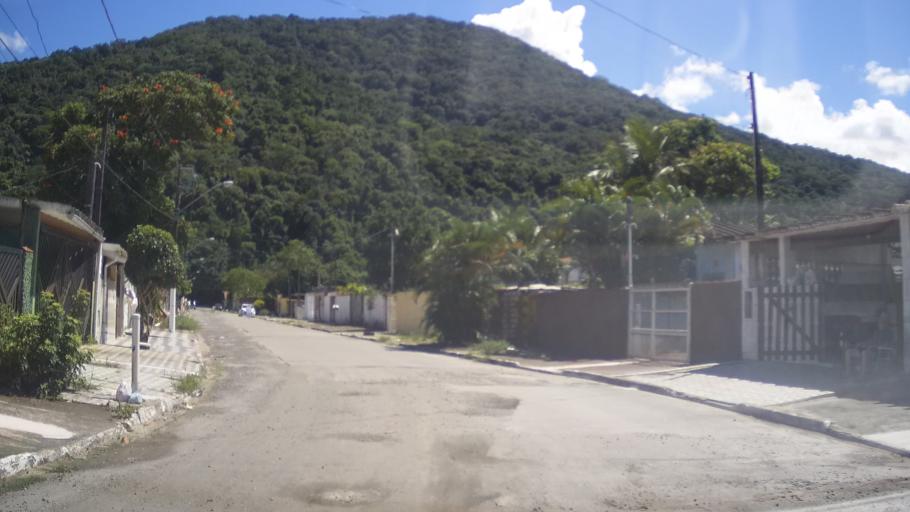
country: BR
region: Sao Paulo
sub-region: Mongagua
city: Mongagua
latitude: -24.0758
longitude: -46.5939
